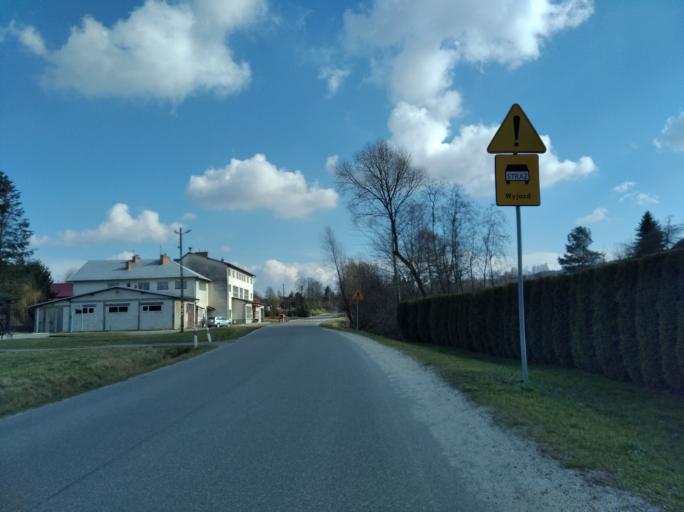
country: PL
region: Subcarpathian Voivodeship
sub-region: Powiat jasielski
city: Kolaczyce
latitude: 49.8536
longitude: 21.4987
